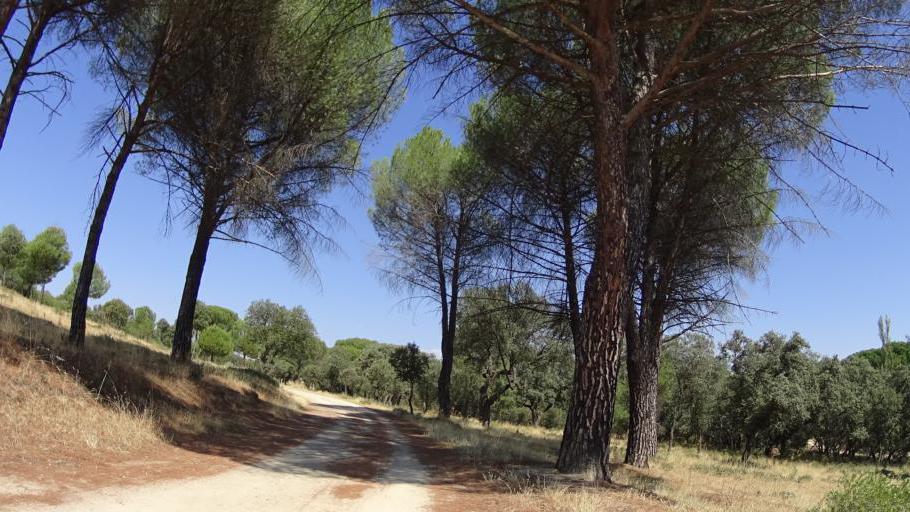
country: ES
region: Madrid
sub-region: Provincia de Madrid
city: Boadilla del Monte
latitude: 40.4273
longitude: -3.8536
